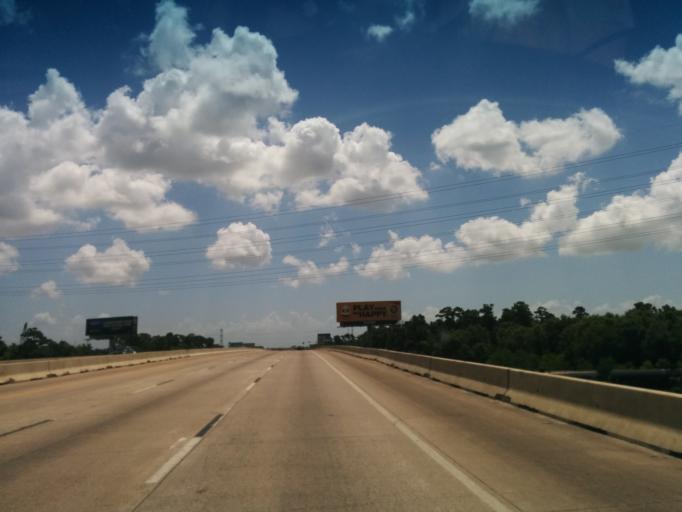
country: US
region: Texas
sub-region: Chambers County
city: Mont Belvieu
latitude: 29.8212
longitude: -94.9164
